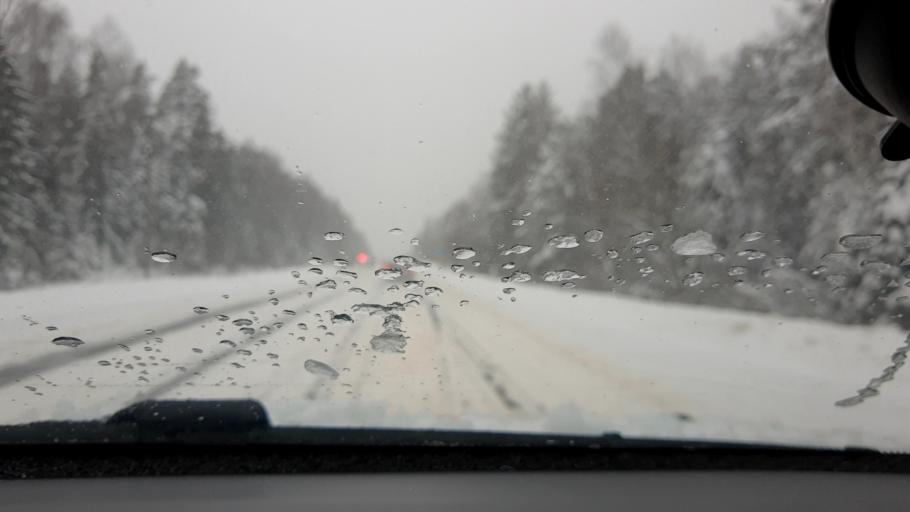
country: RU
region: Nizjnij Novgorod
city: Purekh
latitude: 56.6310
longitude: 43.1803
